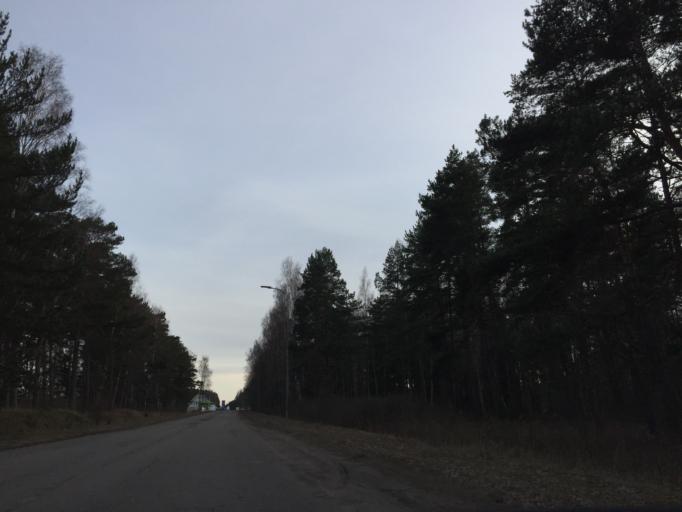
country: LV
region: Salacgrivas
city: Ainazi
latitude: 57.8529
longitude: 24.3552
